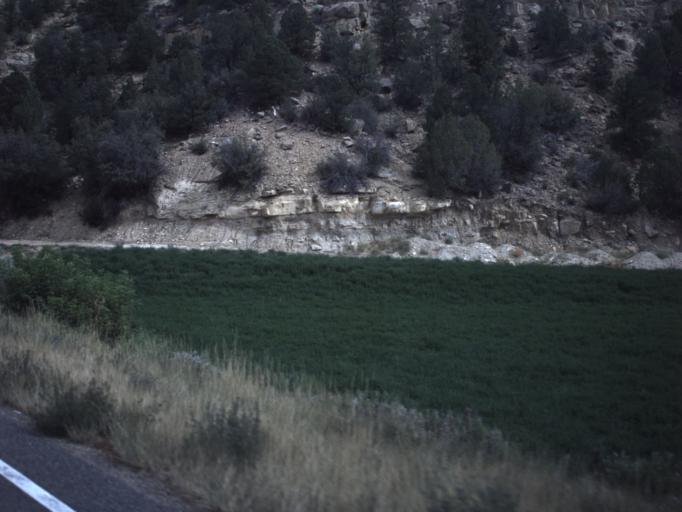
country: US
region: Utah
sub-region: Kane County
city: Kanab
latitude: 37.3294
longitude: -112.5997
